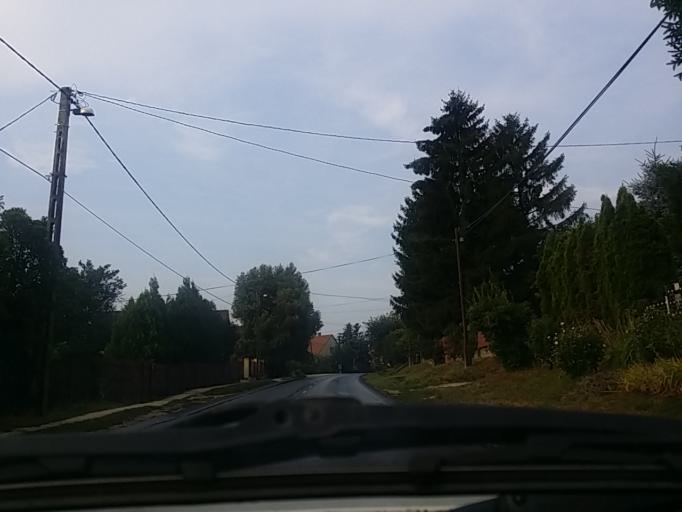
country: HU
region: Pest
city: Zsambek
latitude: 47.5446
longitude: 18.7136
